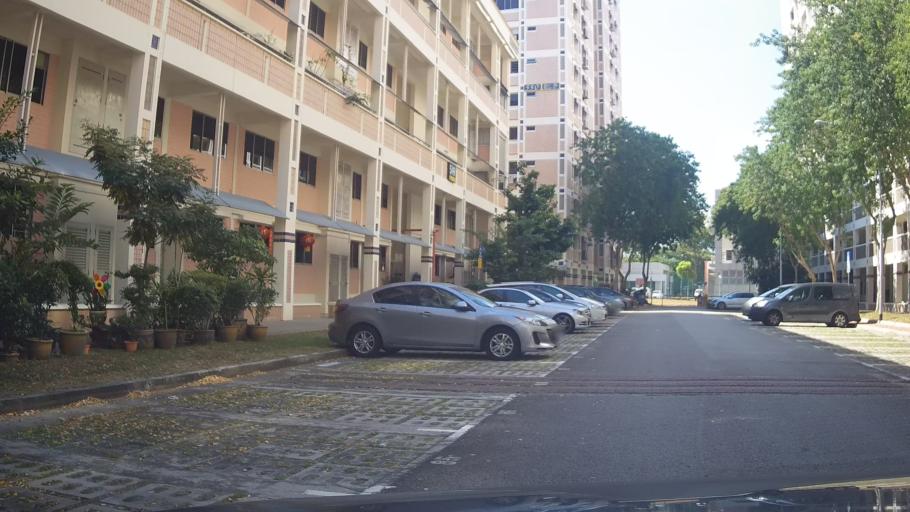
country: MY
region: Johor
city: Kampung Pasir Gudang Baru
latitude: 1.3679
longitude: 103.9534
